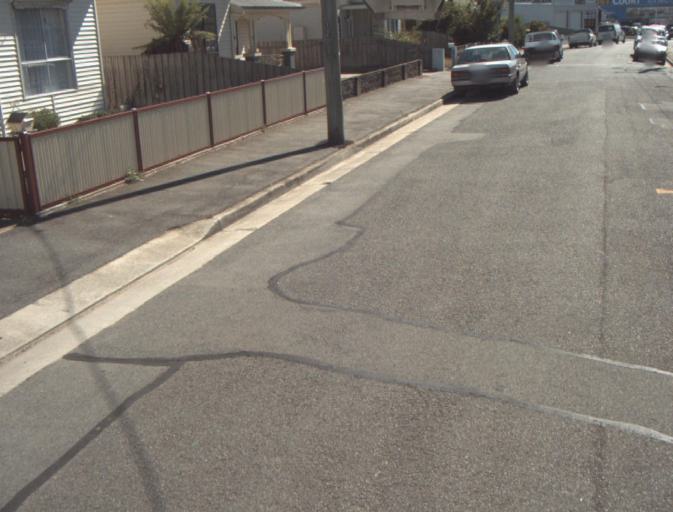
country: AU
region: Tasmania
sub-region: Launceston
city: Newnham
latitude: -41.4135
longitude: 147.1316
